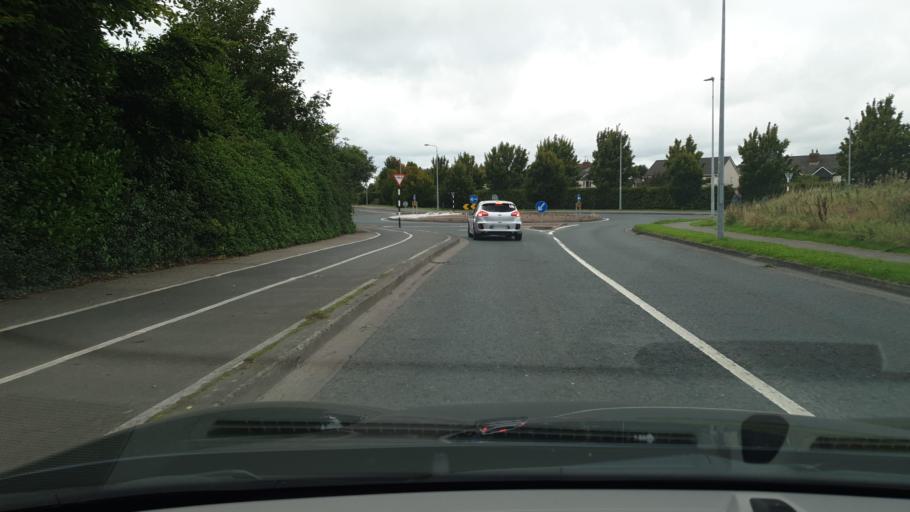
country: IE
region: Leinster
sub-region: Kildare
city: Naas
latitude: 53.2175
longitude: -6.6809
